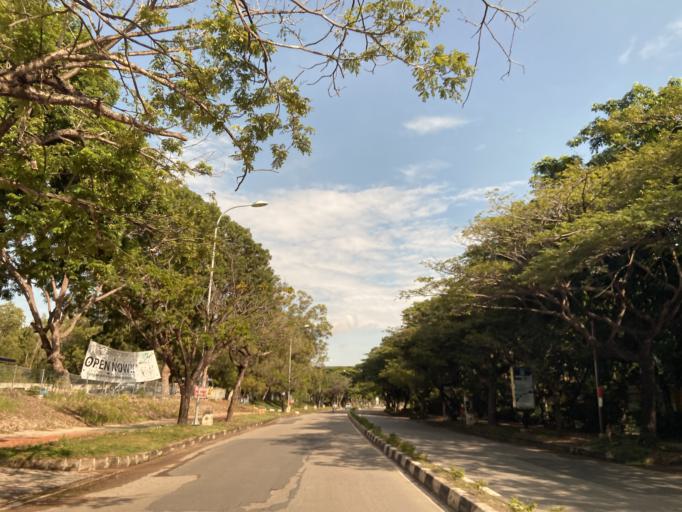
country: SG
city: Singapore
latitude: 1.1279
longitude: 104.0507
